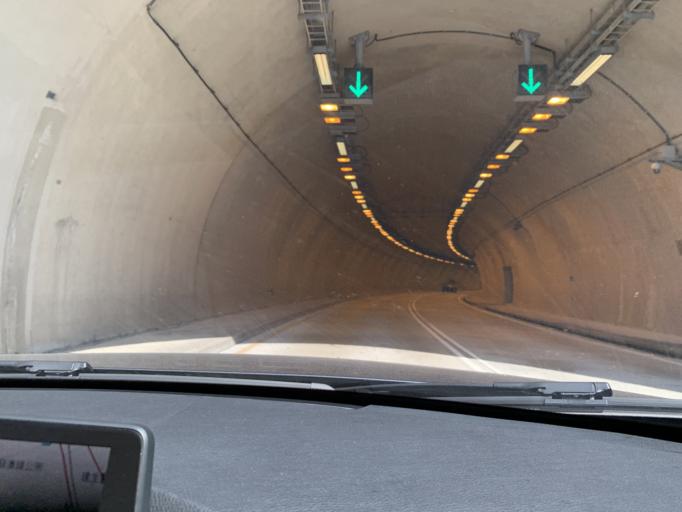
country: TW
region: Taiwan
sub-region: Yilan
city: Yilan
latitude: 24.5918
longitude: 121.8471
